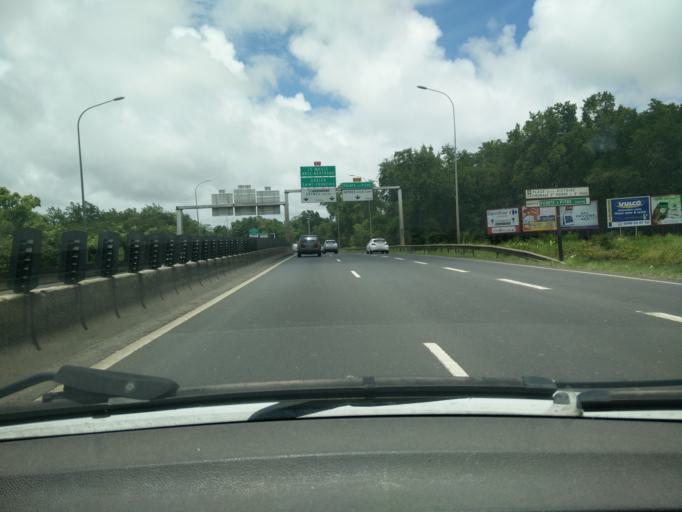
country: GP
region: Guadeloupe
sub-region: Guadeloupe
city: Pointe-a-Pitre
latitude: 16.2531
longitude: -61.5469
